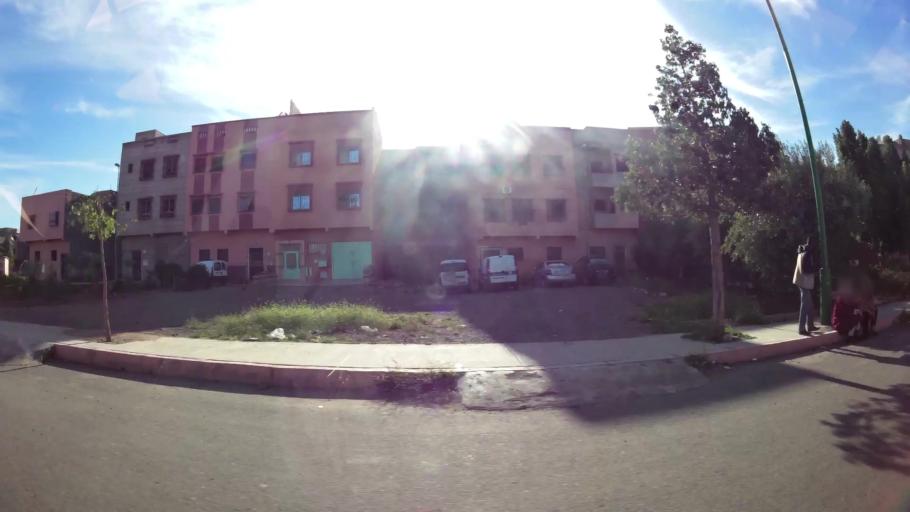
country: MA
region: Marrakech-Tensift-Al Haouz
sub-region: Marrakech
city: Marrakesh
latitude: 31.6879
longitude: -8.0727
